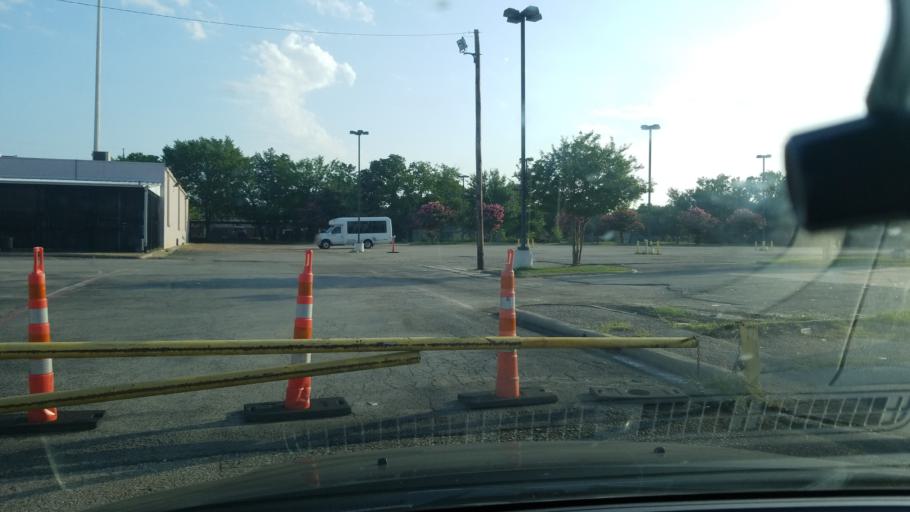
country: US
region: Texas
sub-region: Dallas County
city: Balch Springs
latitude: 32.7179
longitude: -96.6814
